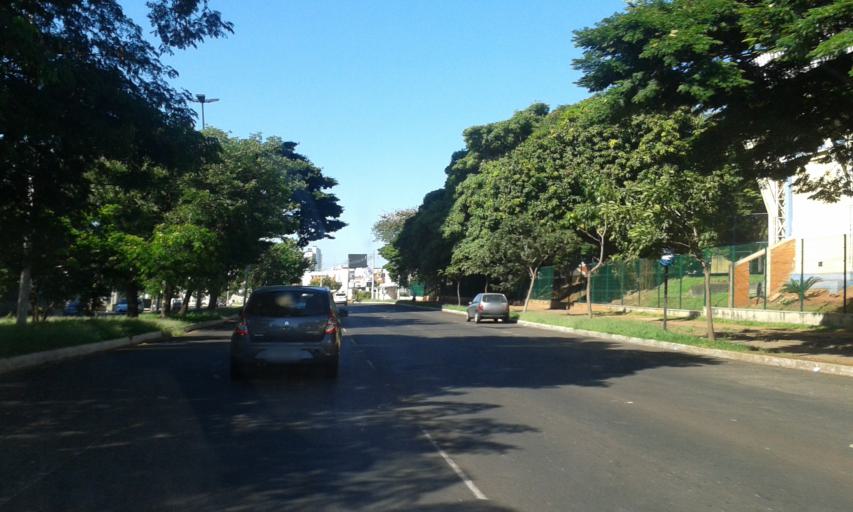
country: BR
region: Minas Gerais
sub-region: Uberlandia
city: Uberlandia
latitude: -18.9080
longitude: -48.2618
